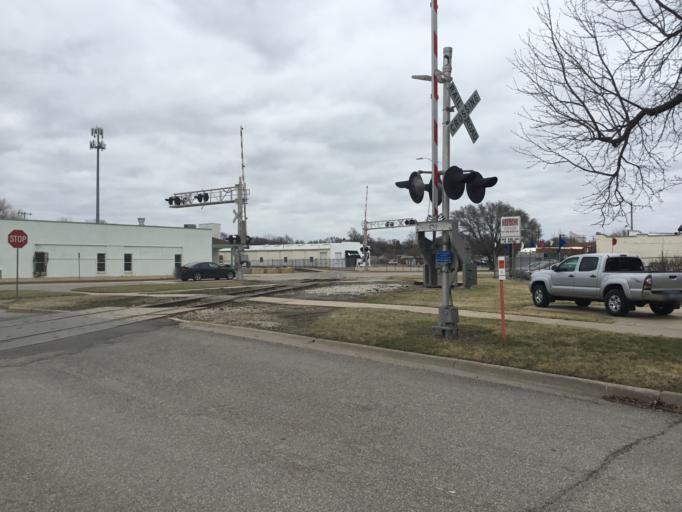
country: US
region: Kansas
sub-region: Sedgwick County
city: Wichita
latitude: 37.6836
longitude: -97.3602
